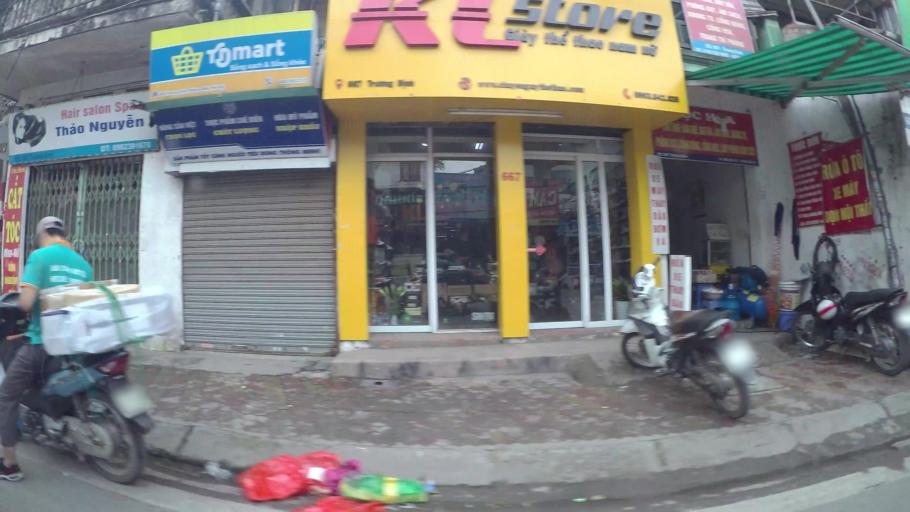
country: VN
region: Ha Noi
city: Van Dien
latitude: 20.9790
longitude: 105.8433
